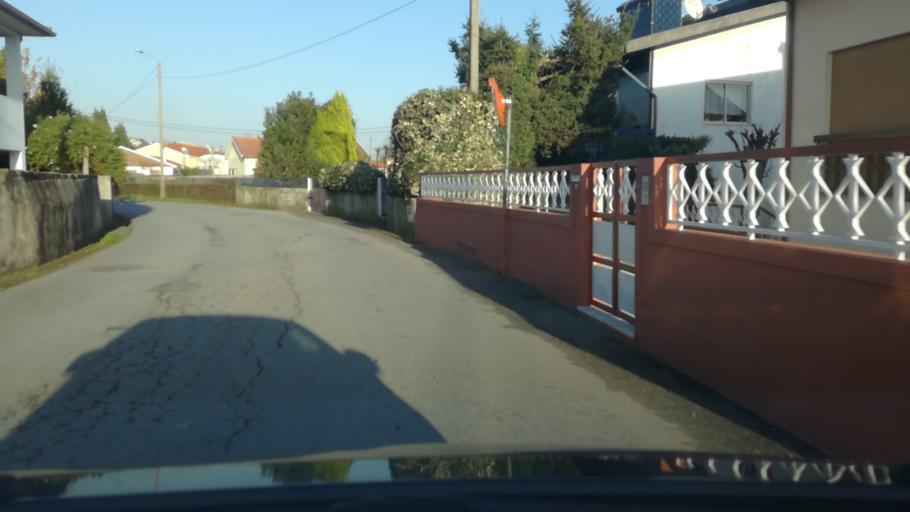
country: PT
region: Braga
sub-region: Vila Nova de Famalicao
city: Ferreiros
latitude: 41.3504
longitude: -8.5237
